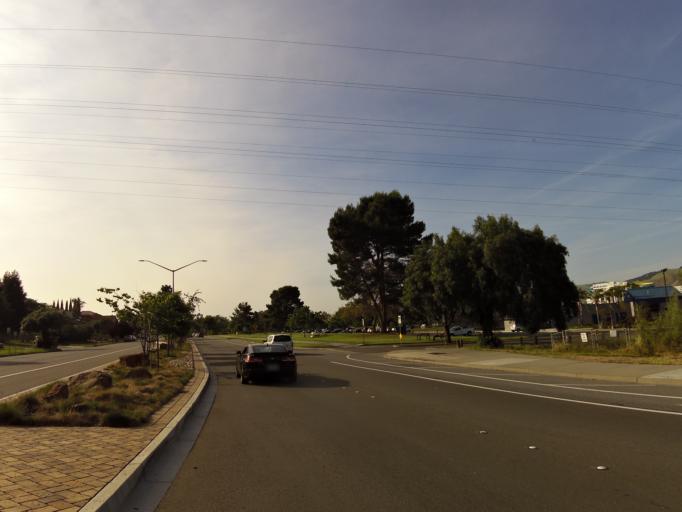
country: US
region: California
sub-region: Alameda County
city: Fremont
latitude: 37.5417
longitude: -121.9608
